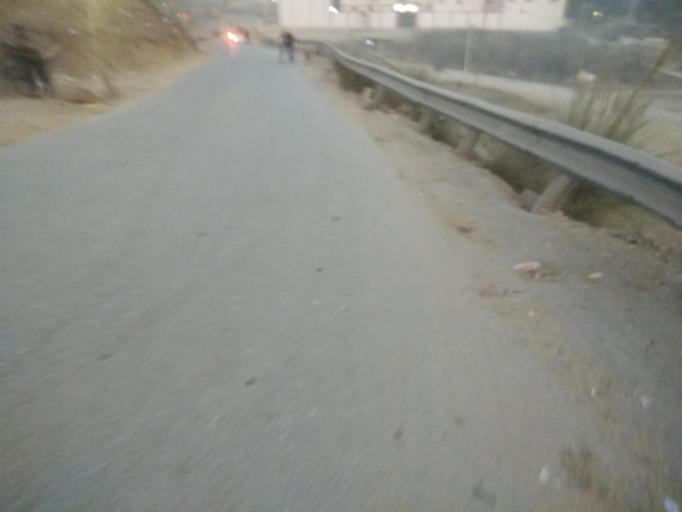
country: IN
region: Uttar Pradesh
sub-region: Varanasi
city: Ramnagar
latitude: 25.2538
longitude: 83.0204
